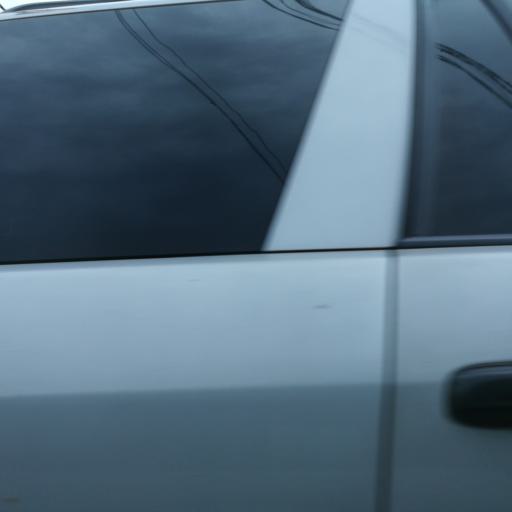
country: NG
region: Lagos
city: Ikeja
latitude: 6.6012
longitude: 3.3461
